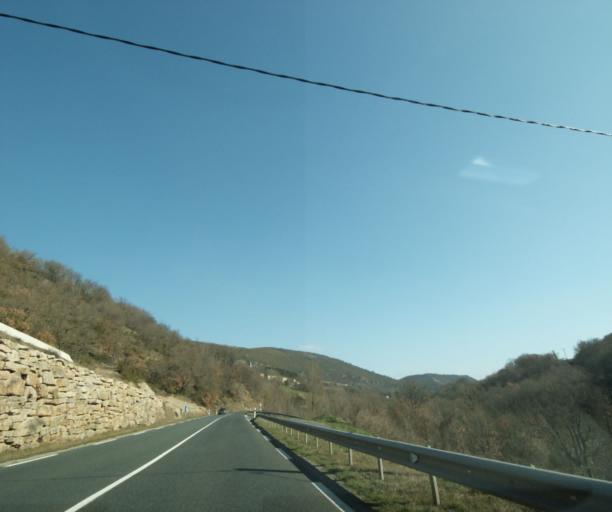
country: FR
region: Midi-Pyrenees
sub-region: Departement de l'Aveyron
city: Saint-Affrique
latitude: 43.9486
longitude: 2.9121
